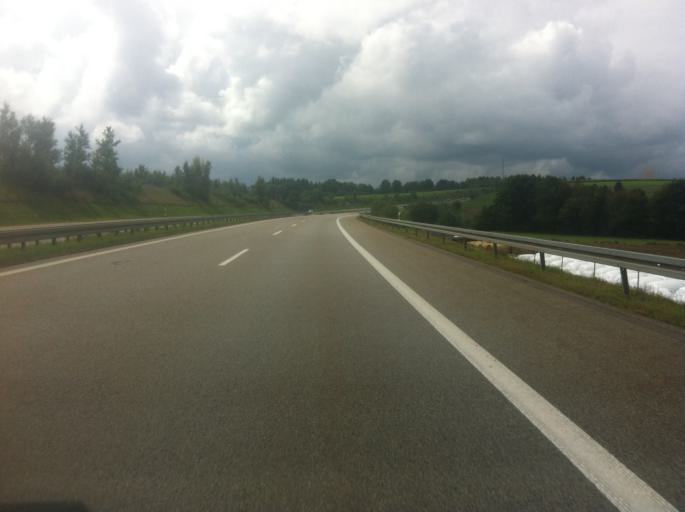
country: DE
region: Bavaria
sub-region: Upper Palatinate
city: Vohenstrauss
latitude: 49.6002
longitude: 12.3222
